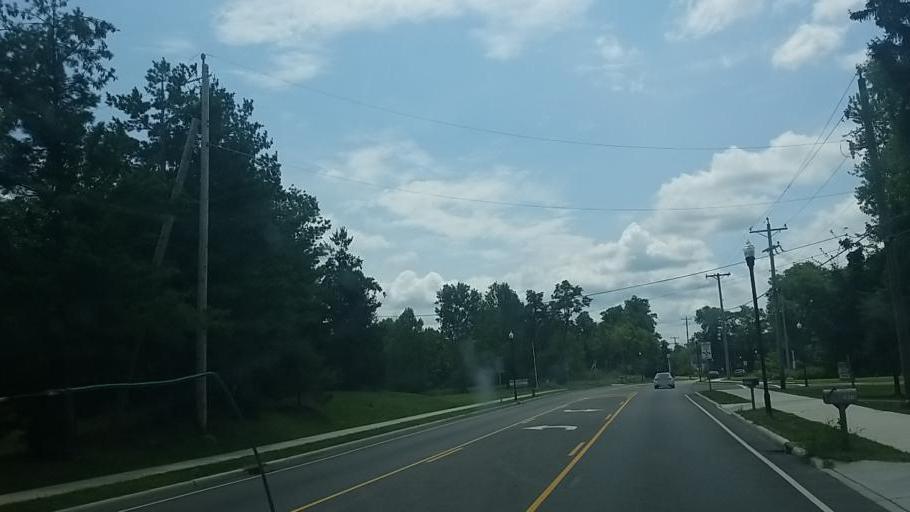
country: US
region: Ohio
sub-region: Franklin County
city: Reynoldsburg
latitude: 39.9425
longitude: -82.7726
